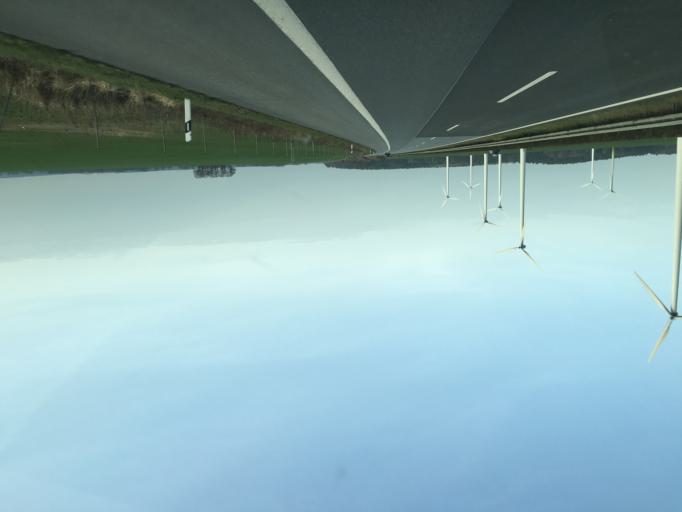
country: DE
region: Brandenburg
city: Wittstock
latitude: 53.2098
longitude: 12.4508
